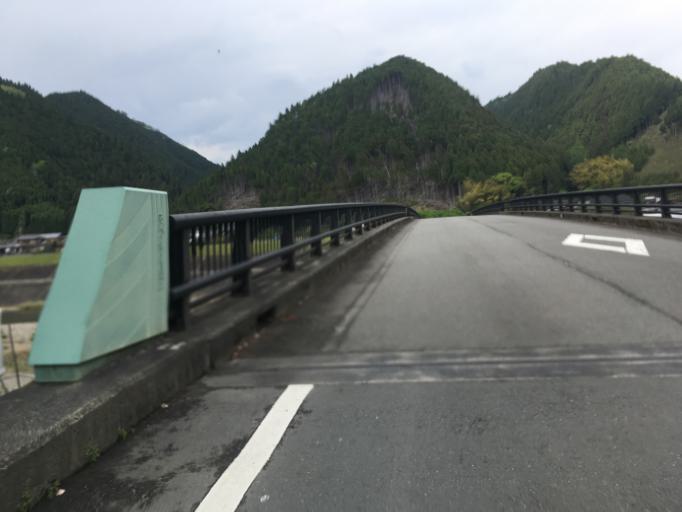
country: JP
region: Kyoto
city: Kameoka
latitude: 35.1451
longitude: 135.5741
